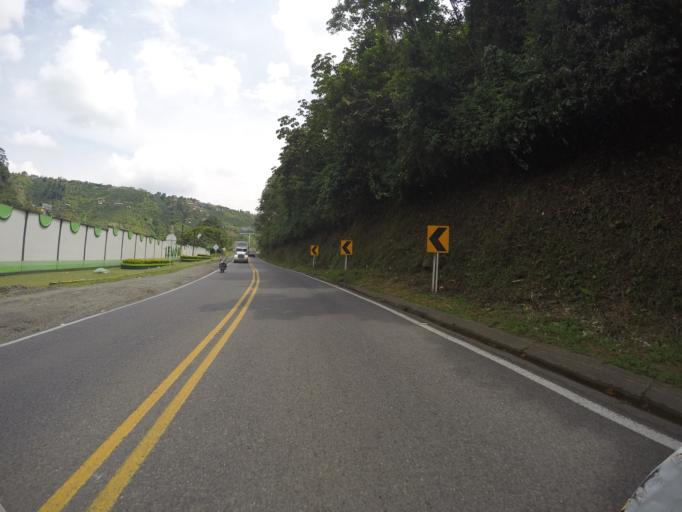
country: CO
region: Risaralda
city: Pereira
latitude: 4.7873
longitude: -75.6943
